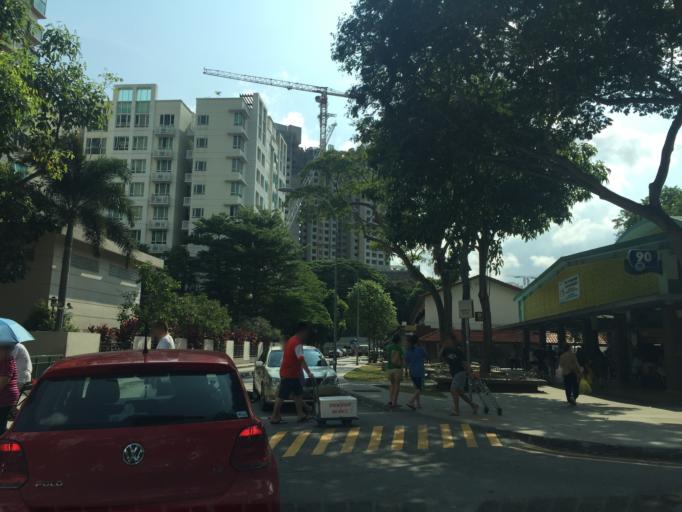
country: SG
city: Singapore
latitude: 1.3231
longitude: 103.8545
